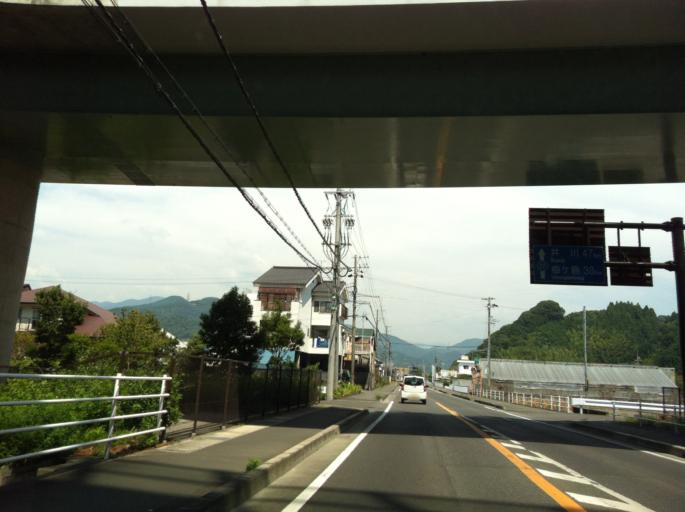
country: JP
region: Shizuoka
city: Shizuoka-shi
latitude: 35.0419
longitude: 138.3784
